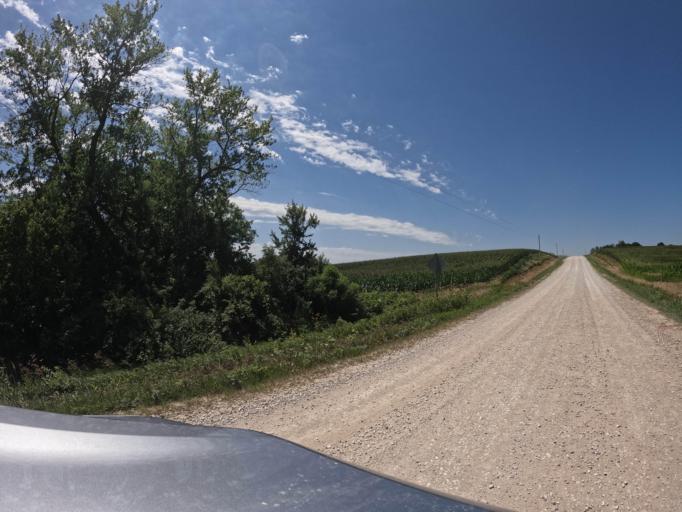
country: US
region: Iowa
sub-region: Keokuk County
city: Sigourney
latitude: 41.4667
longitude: -92.3580
